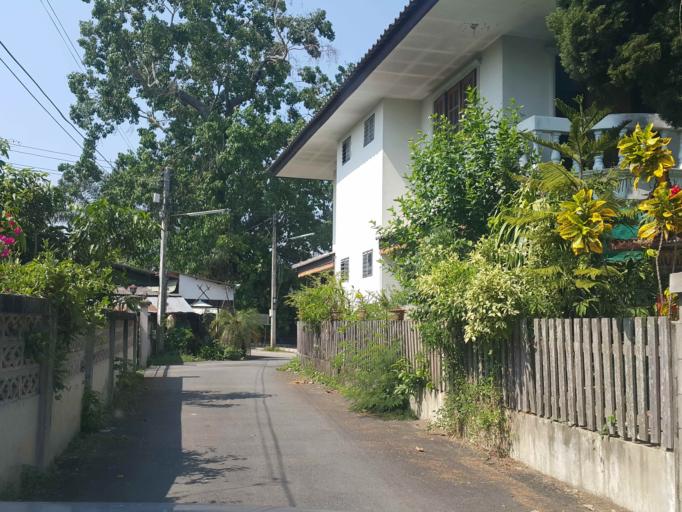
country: TH
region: Chiang Mai
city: Saraphi
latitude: 18.7731
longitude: 99.0540
